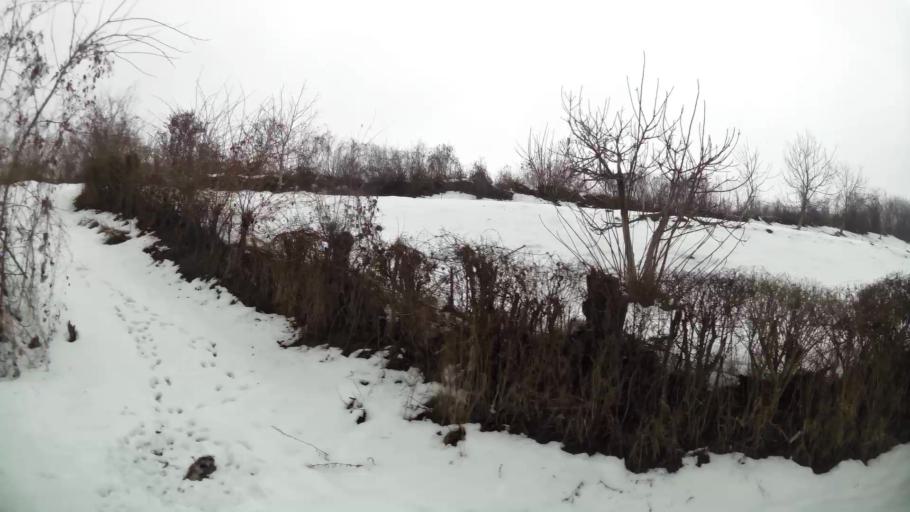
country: RS
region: Central Serbia
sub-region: Belgrade
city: Zvezdara
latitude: 44.7486
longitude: 20.5173
